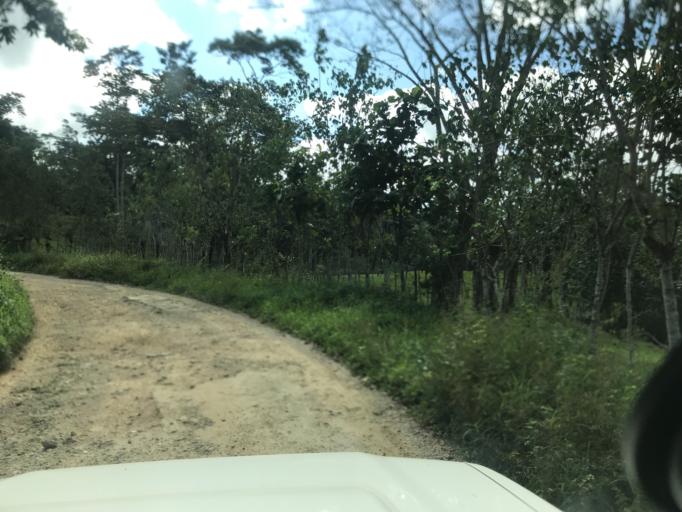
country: VU
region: Sanma
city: Luganville
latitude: -15.4734
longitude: 167.0729
